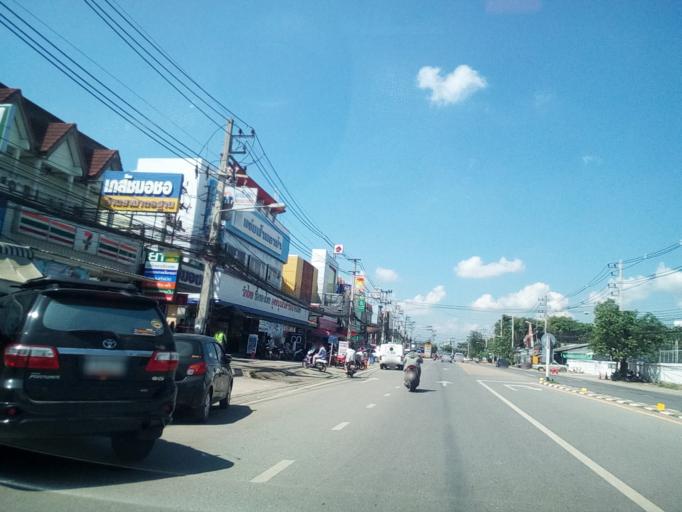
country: TH
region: Lamphun
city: Lamphun
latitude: 18.5872
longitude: 99.0491
